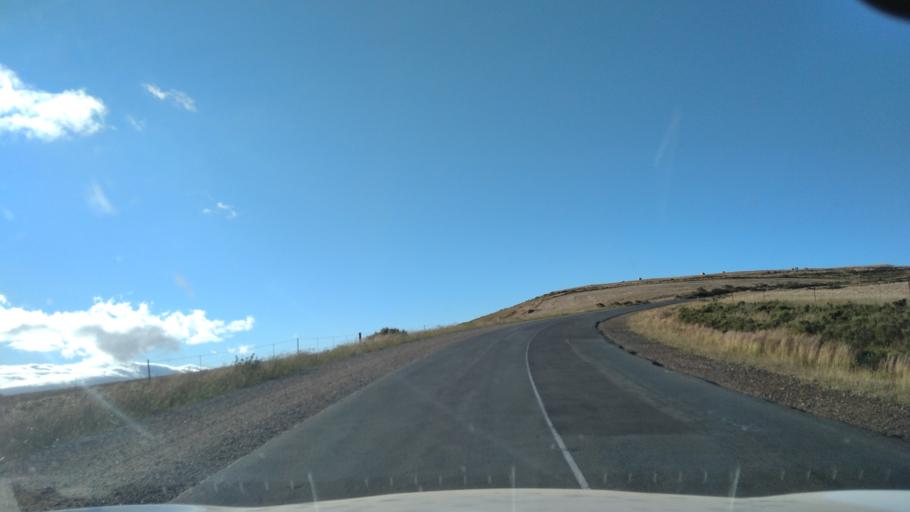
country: ZA
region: Western Cape
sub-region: Overberg District Municipality
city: Caledon
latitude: -34.1546
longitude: 19.3021
